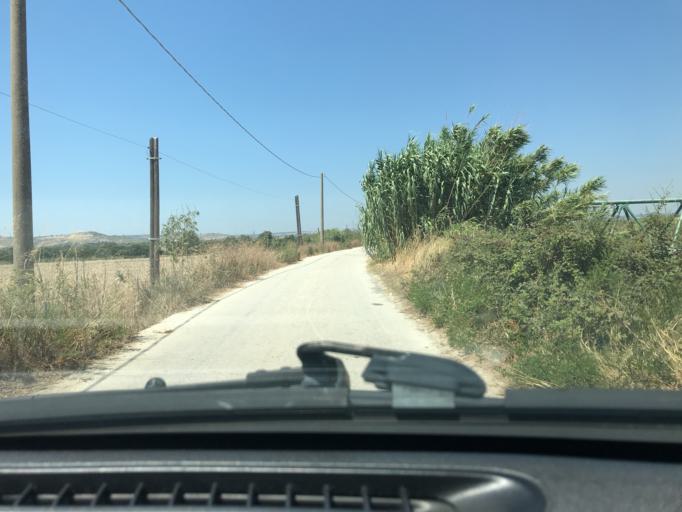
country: IT
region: Sicily
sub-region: Provincia di Siracusa
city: Noto
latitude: 36.8359
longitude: 15.0550
